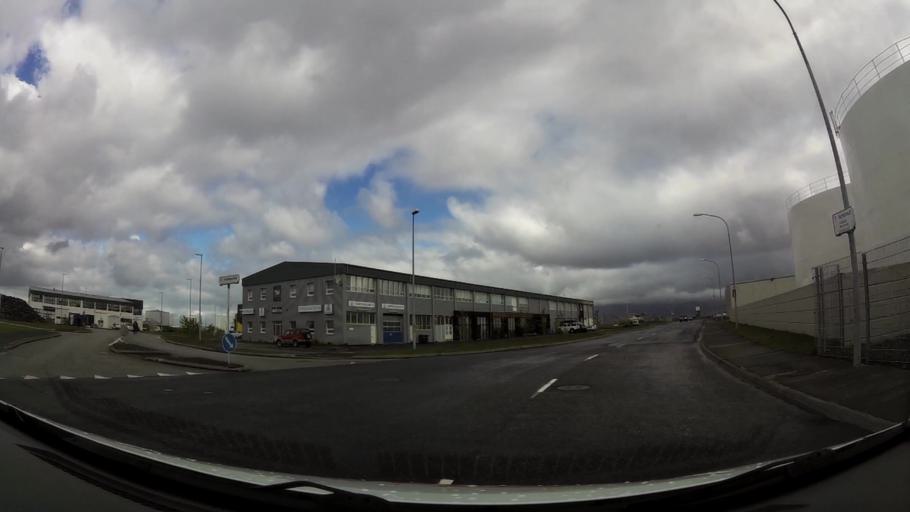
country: IS
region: Capital Region
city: Reykjavik
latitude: 64.1562
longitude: -21.9412
